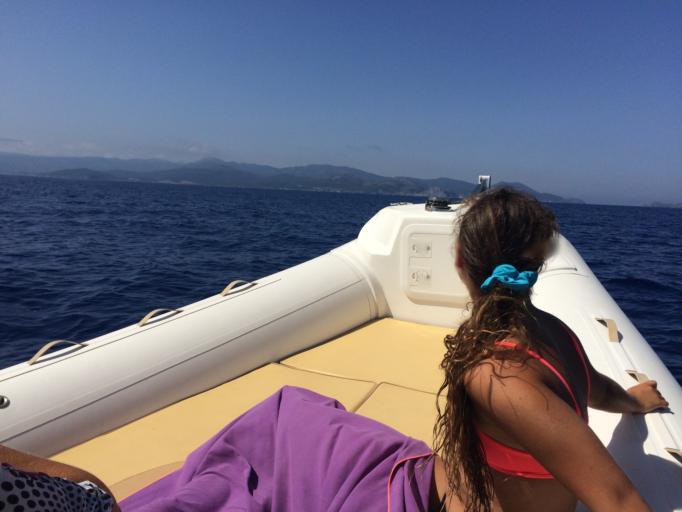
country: FR
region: Corsica
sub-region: Departement de la Haute-Corse
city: Brando
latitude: 43.0348
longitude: 9.4970
